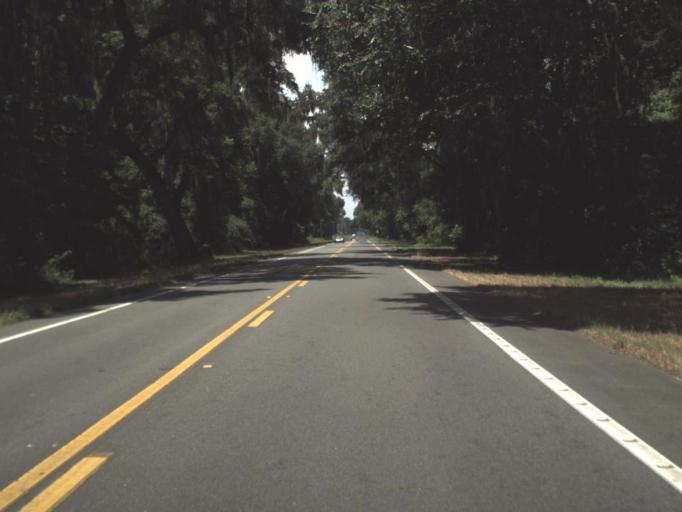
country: US
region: Florida
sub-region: Alachua County
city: Archer
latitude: 29.5259
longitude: -82.4054
